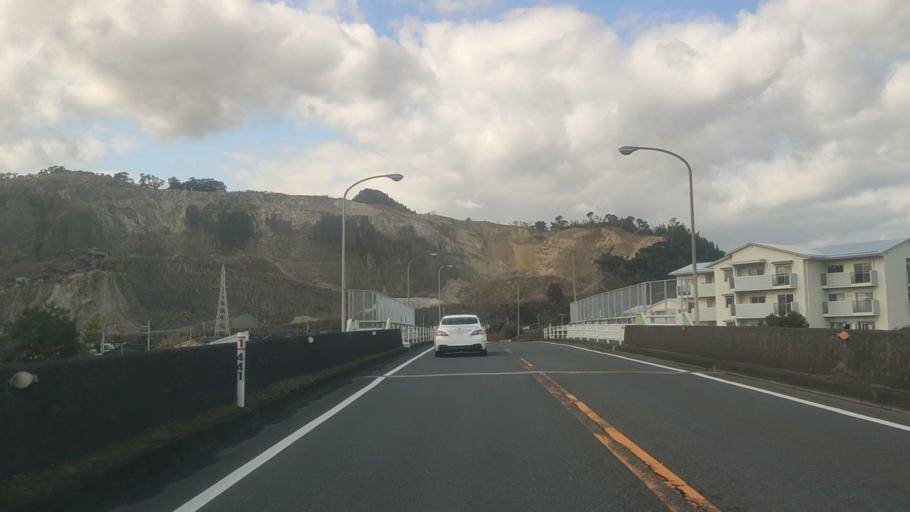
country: JP
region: Kagoshima
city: Kajiki
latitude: 31.7363
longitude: 130.6527
